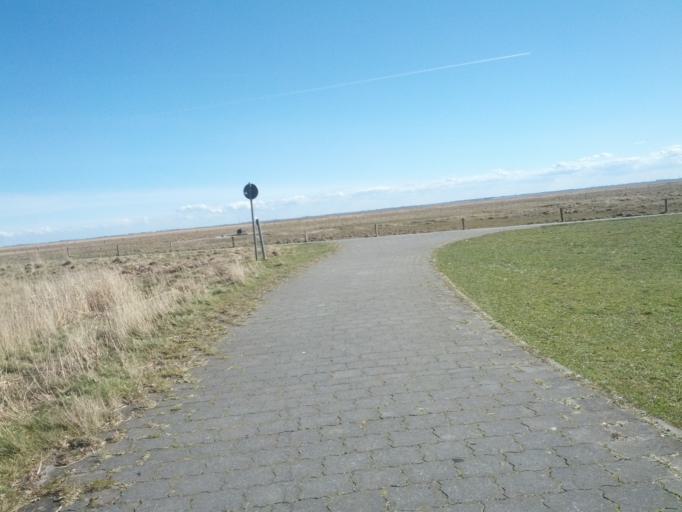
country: DE
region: Lower Saxony
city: Langeoog
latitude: 53.7500
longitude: 7.5327
